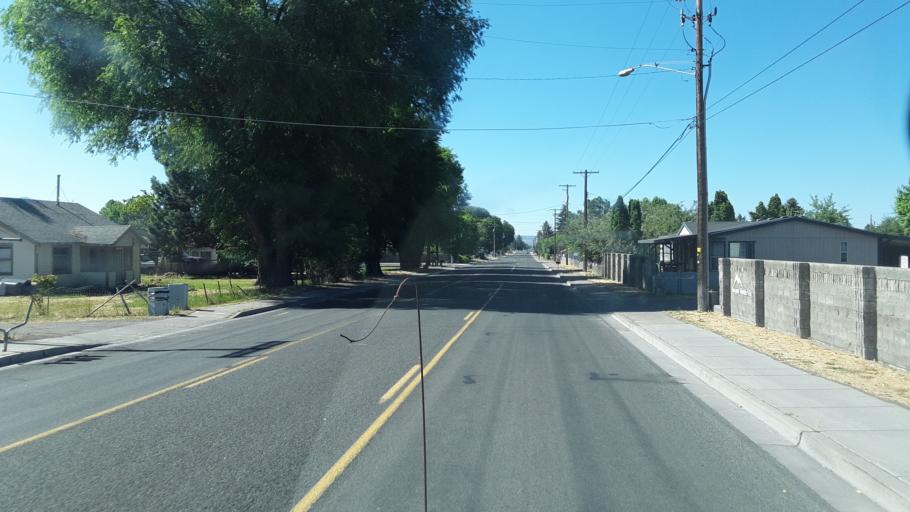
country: US
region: Oregon
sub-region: Klamath County
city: Altamont
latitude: 42.1906
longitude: -121.7228
